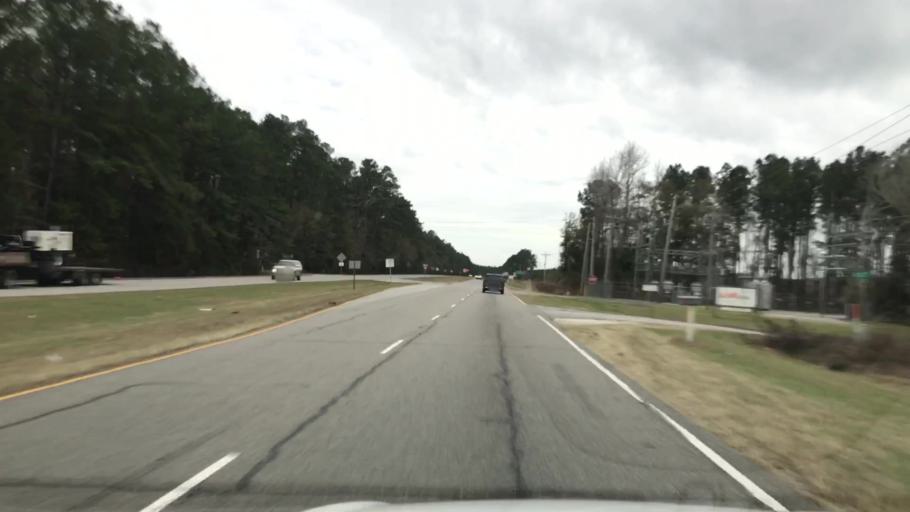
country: US
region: South Carolina
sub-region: Georgetown County
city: Georgetown
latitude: 33.2937
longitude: -79.3469
